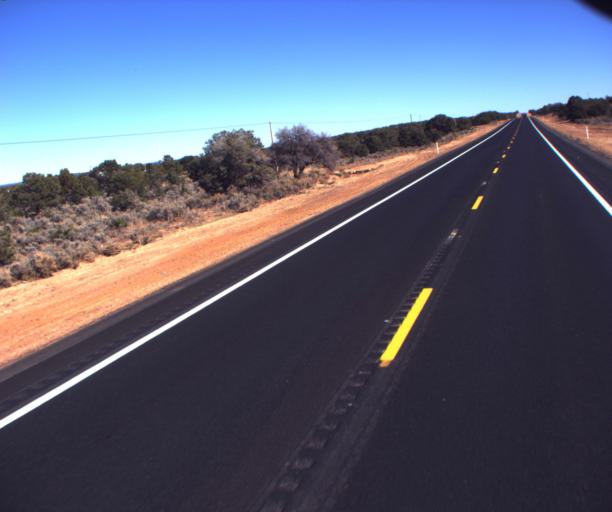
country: US
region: Arizona
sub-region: Apache County
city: Ganado
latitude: 35.7180
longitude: -109.3965
